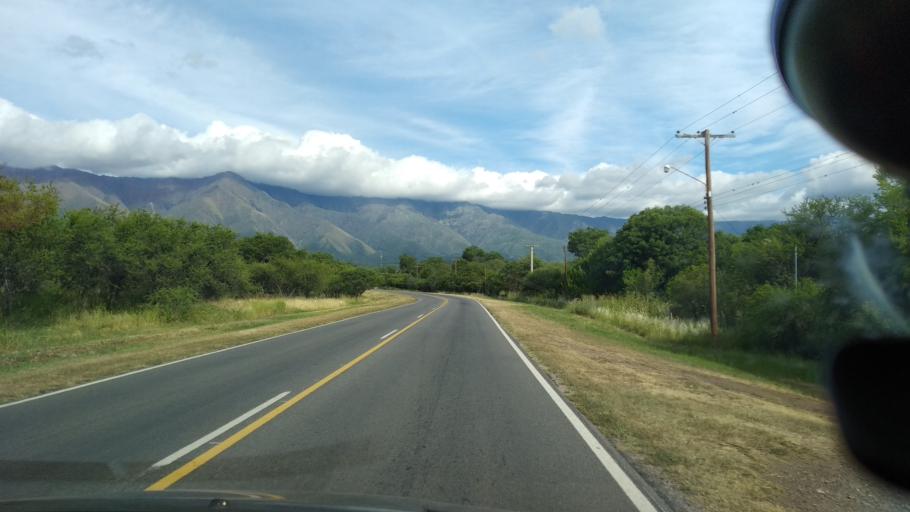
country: AR
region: Cordoba
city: Villa Las Rosas
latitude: -32.0096
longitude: -65.0525
